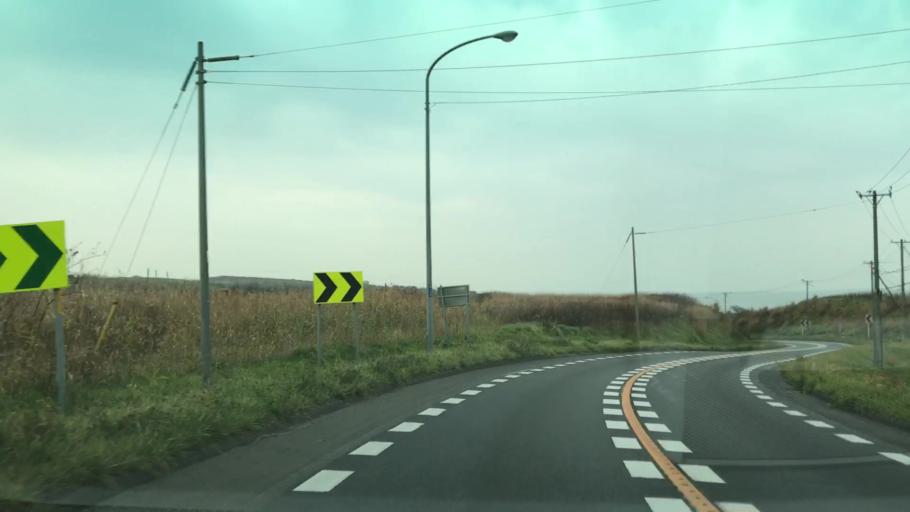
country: JP
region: Hokkaido
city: Ishikari
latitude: 43.3611
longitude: 141.4308
